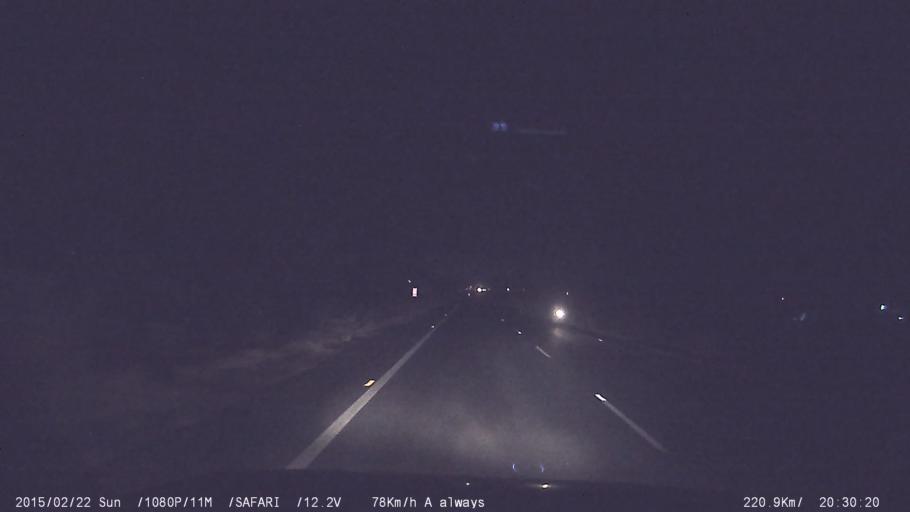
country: IN
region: Tamil Nadu
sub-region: Dindigul
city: Dindigul
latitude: 10.3383
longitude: 77.9374
